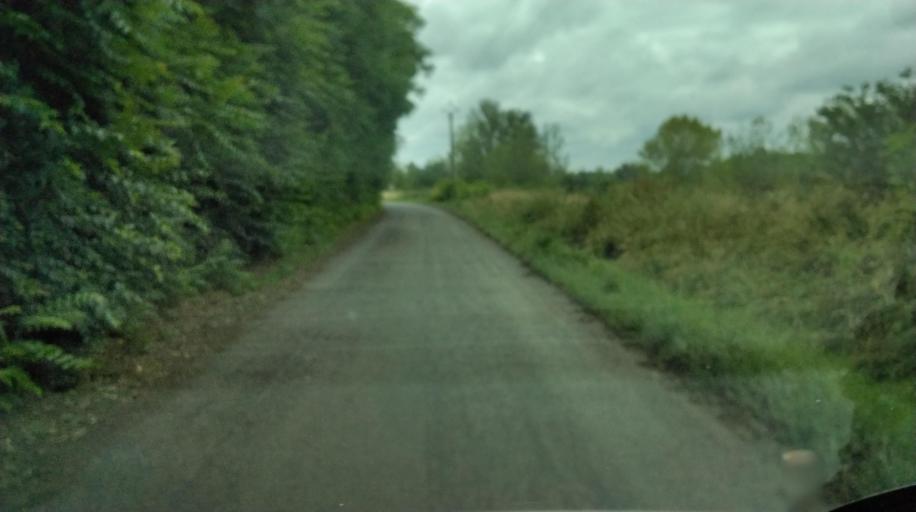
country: FR
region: Midi-Pyrenees
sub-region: Departement de la Haute-Garonne
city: Martres-Tolosane
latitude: 43.2085
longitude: 1.0432
